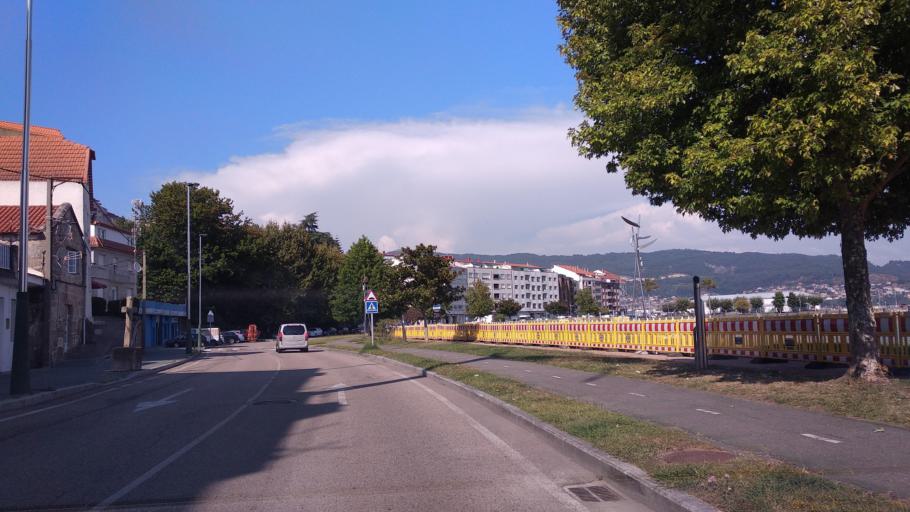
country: ES
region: Galicia
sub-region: Provincia de Pontevedra
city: Moana
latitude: 42.2725
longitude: -8.7404
